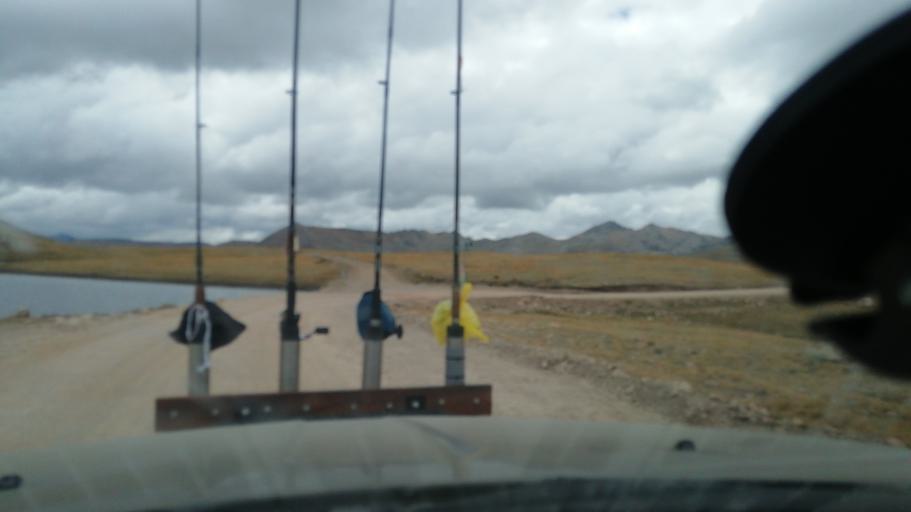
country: PE
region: Huancavelica
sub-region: Provincia de Huancavelica
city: Acobambilla
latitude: -12.5430
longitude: -75.5472
